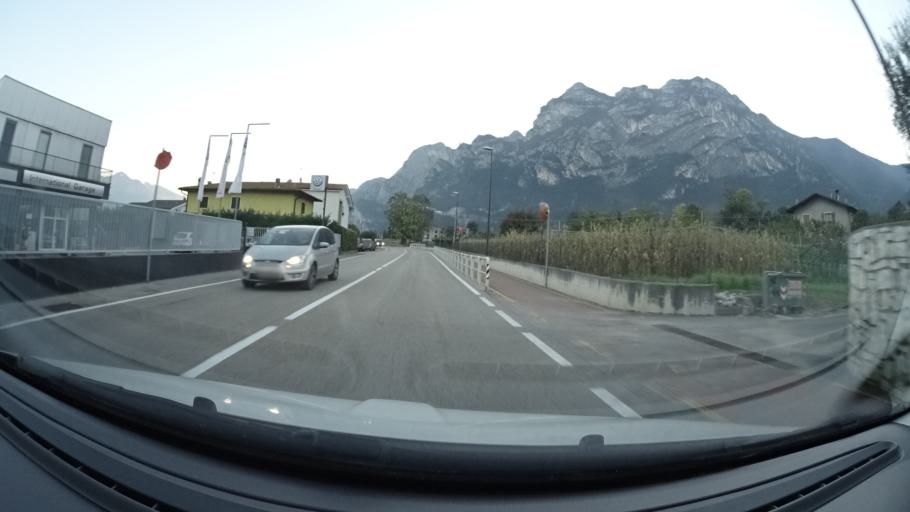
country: IT
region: Trentino-Alto Adige
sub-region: Provincia di Trento
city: Riva del Garda
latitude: 45.8898
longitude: 10.8557
